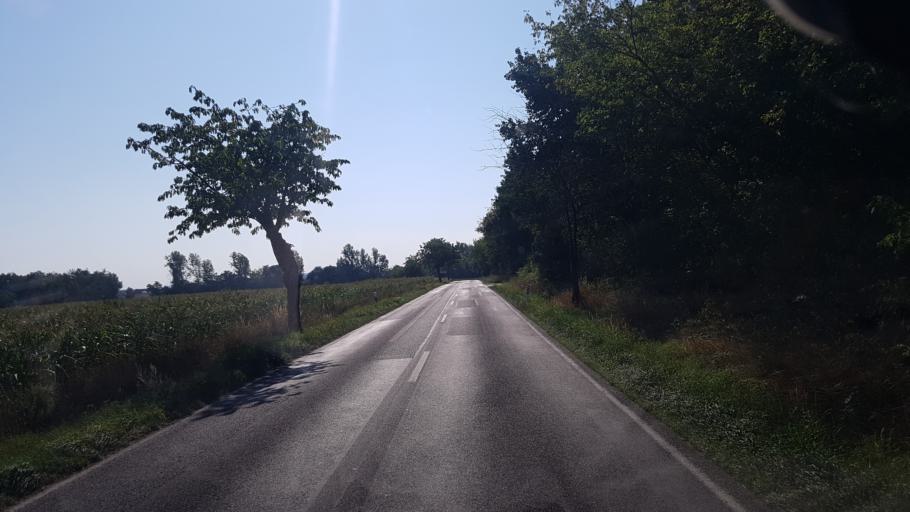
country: DE
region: Brandenburg
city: Hirschfeld
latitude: 51.3938
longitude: 13.6054
